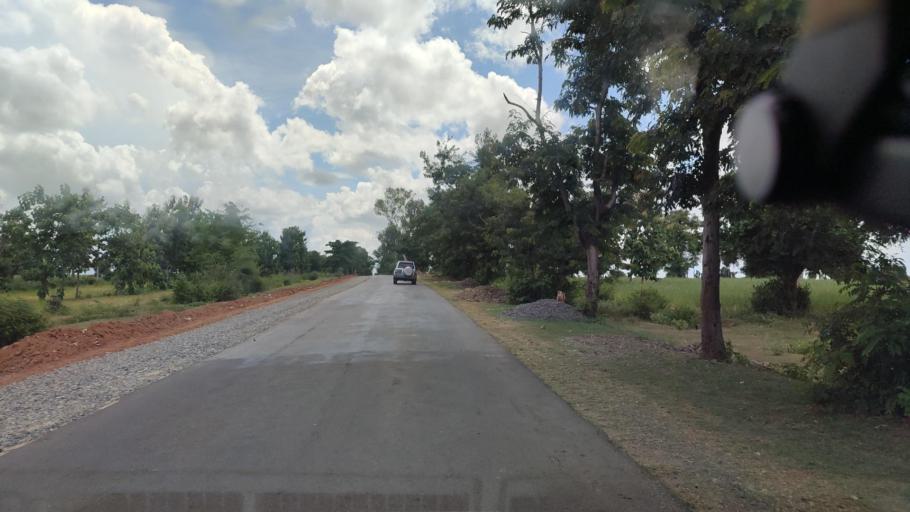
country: MM
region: Magway
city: Magway
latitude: 20.1944
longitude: 95.0716
